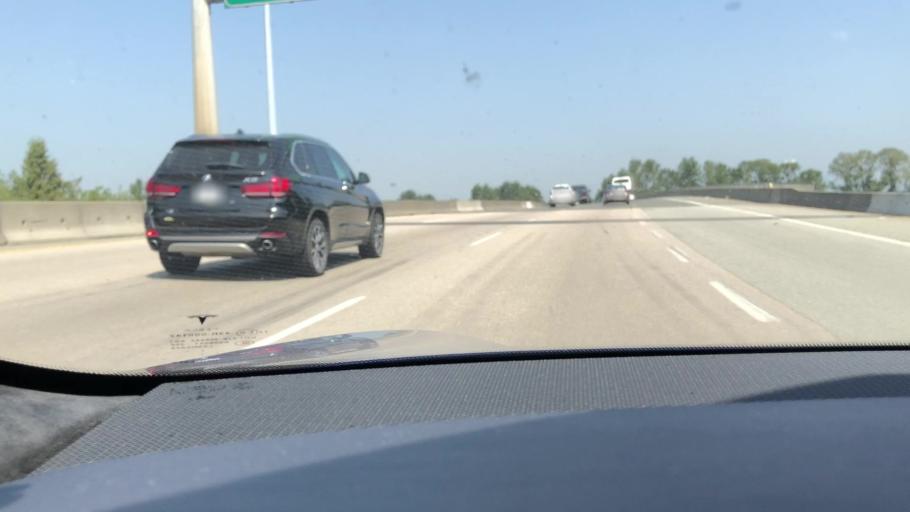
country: CA
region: British Columbia
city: New Westminster
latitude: 49.1741
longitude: -122.9548
